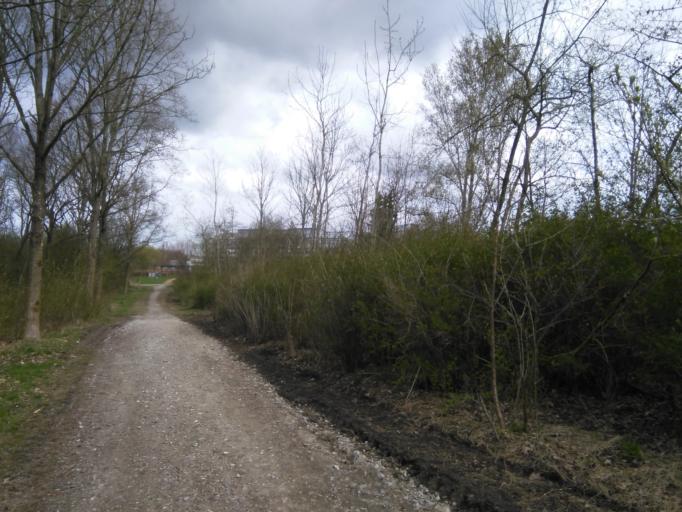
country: DK
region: Central Jutland
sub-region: Arhus Kommune
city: Stavtrup
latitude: 56.1694
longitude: 10.1316
